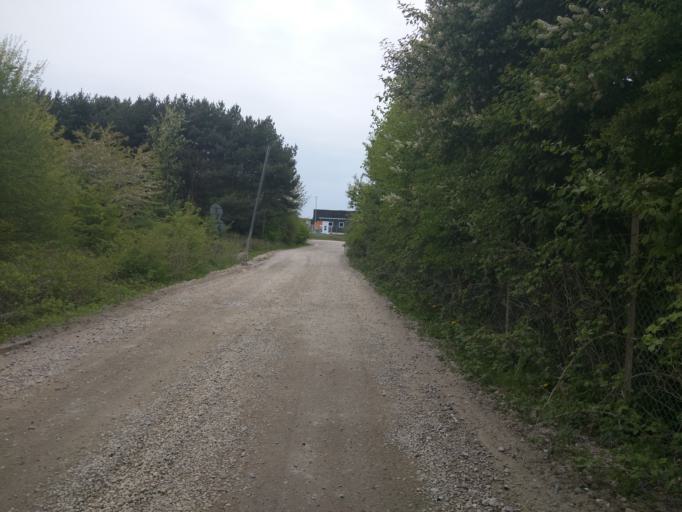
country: DK
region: South Denmark
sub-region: Fredericia Kommune
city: Snoghoj
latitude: 55.5338
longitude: 9.7072
